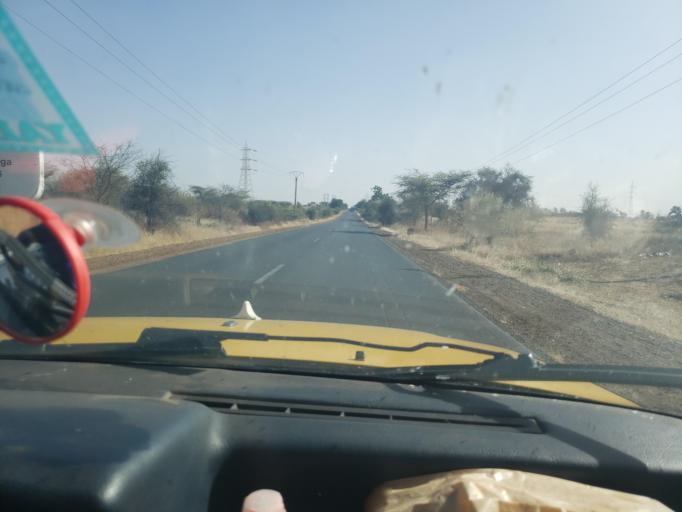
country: SN
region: Louga
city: Louga
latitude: 15.6564
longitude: -16.2565
